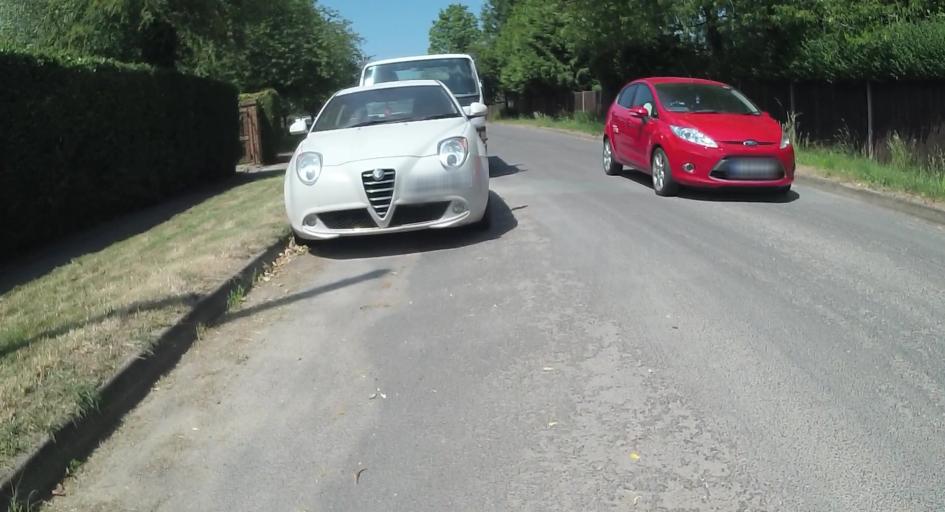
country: GB
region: England
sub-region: Hampshire
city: Basingstoke
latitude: 51.2954
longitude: -1.1106
